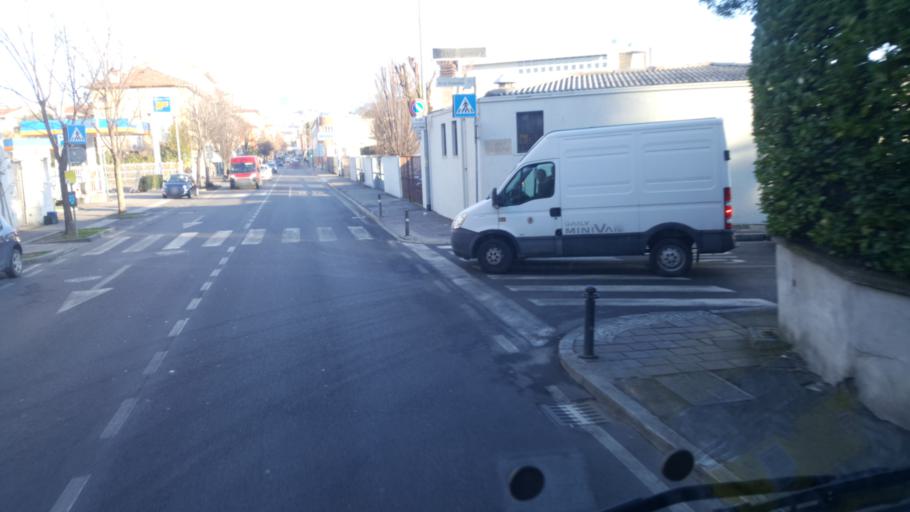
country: IT
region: Lombardy
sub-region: Provincia di Bergamo
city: Bergamo
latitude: 45.6815
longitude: 9.6621
